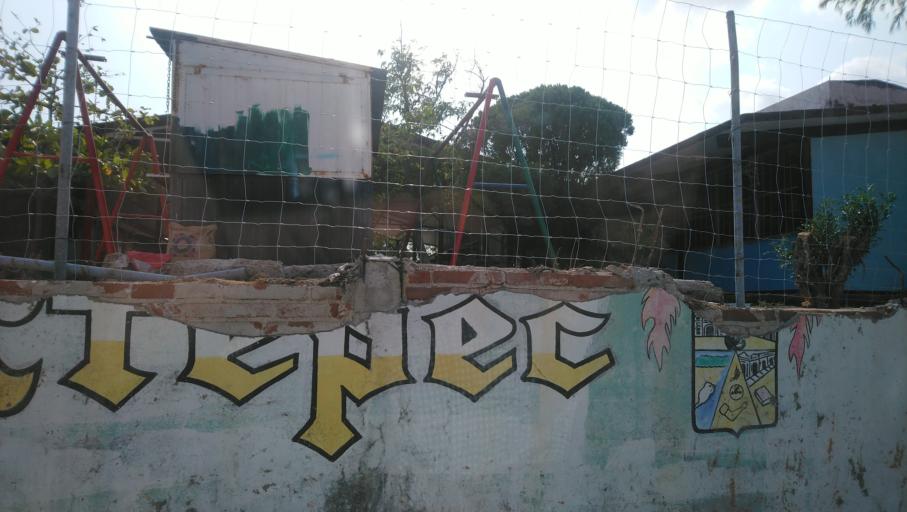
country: MX
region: Oaxaca
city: San Jeronimo Ixtepec
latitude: 16.5639
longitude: -95.0981
